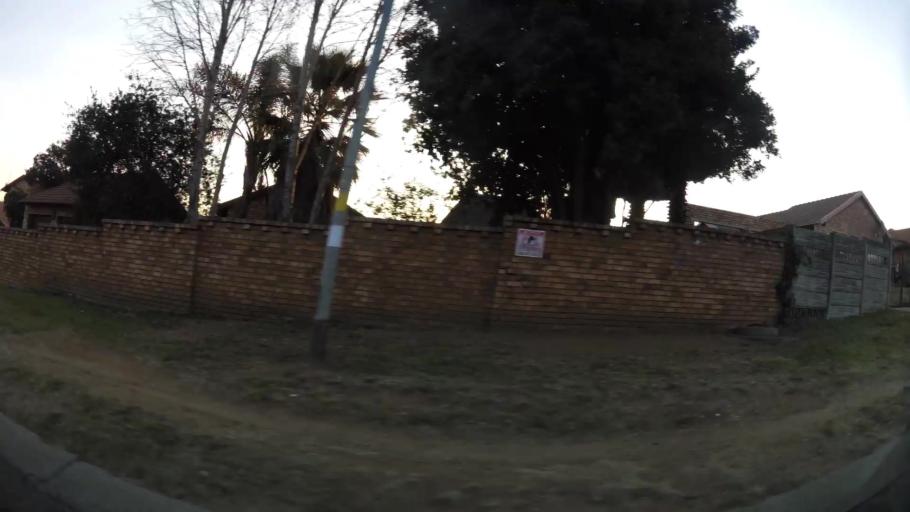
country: ZA
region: Gauteng
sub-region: City of Johannesburg Metropolitan Municipality
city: Modderfontein
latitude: -26.0726
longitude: 28.2255
